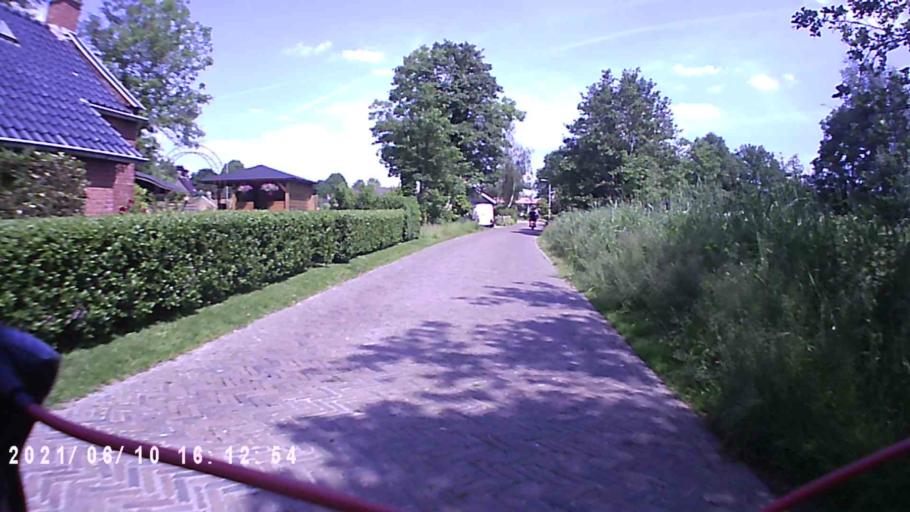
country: NL
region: Friesland
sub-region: Gemeente Achtkarspelen
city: Kootstertille
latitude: 53.2124
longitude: 6.0614
